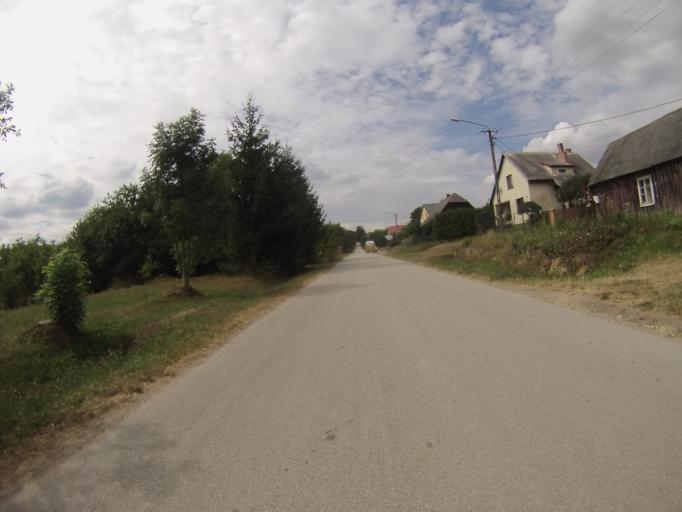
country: PL
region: Swietokrzyskie
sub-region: Powiat kielecki
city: Lagow
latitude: 50.7418
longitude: 21.1126
